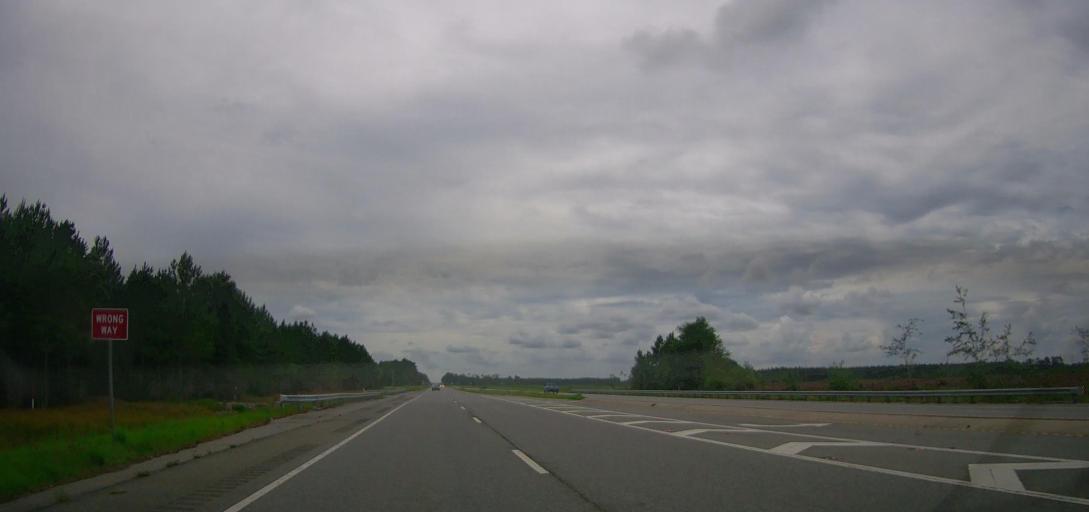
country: US
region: Georgia
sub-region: Appling County
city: Baxley
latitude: 31.7560
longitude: -82.2831
